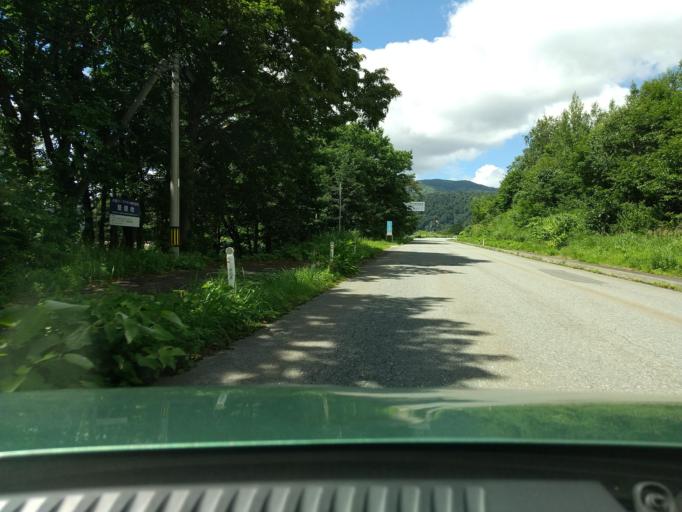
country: JP
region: Iwate
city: Shizukuishi
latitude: 39.7759
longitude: 140.7631
